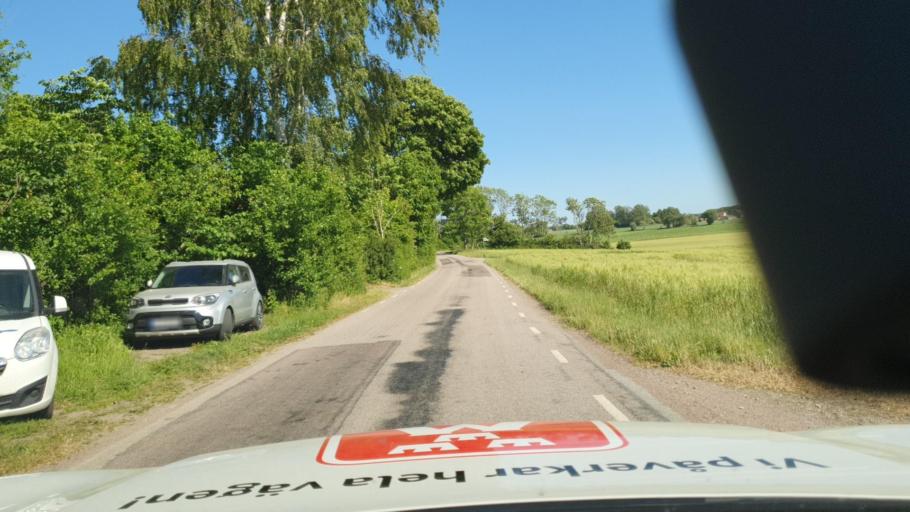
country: SE
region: Skane
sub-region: Sjobo Kommun
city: Sjoebo
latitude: 55.6379
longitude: 13.7980
